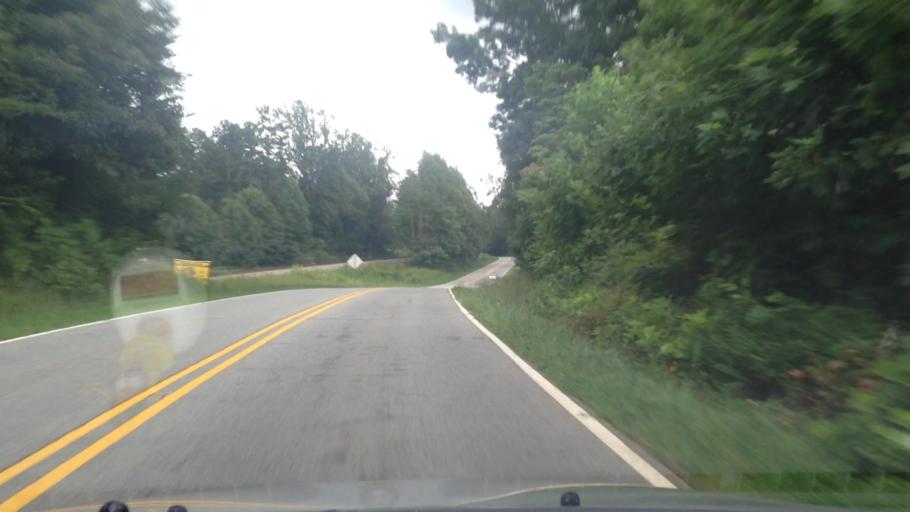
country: US
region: North Carolina
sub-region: Forsyth County
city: Walkertown
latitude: 36.2027
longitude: -80.1670
